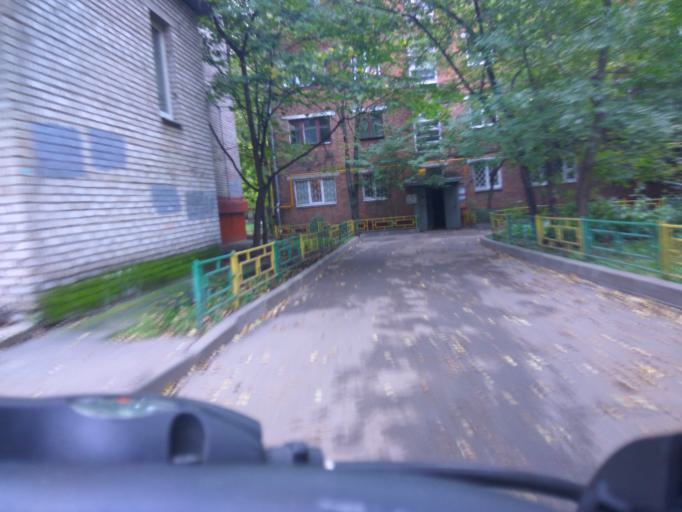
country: RU
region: Moscow
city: Altuf'yevskiy
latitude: 55.8806
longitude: 37.5775
